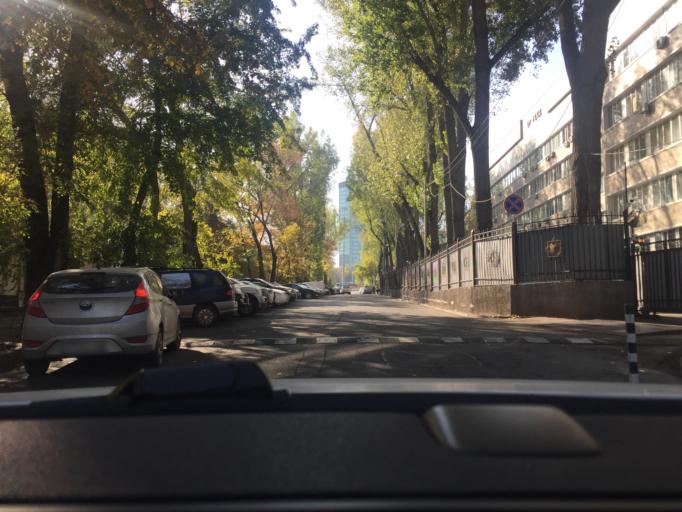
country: KZ
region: Almaty Qalasy
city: Almaty
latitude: 43.2425
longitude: 76.9142
